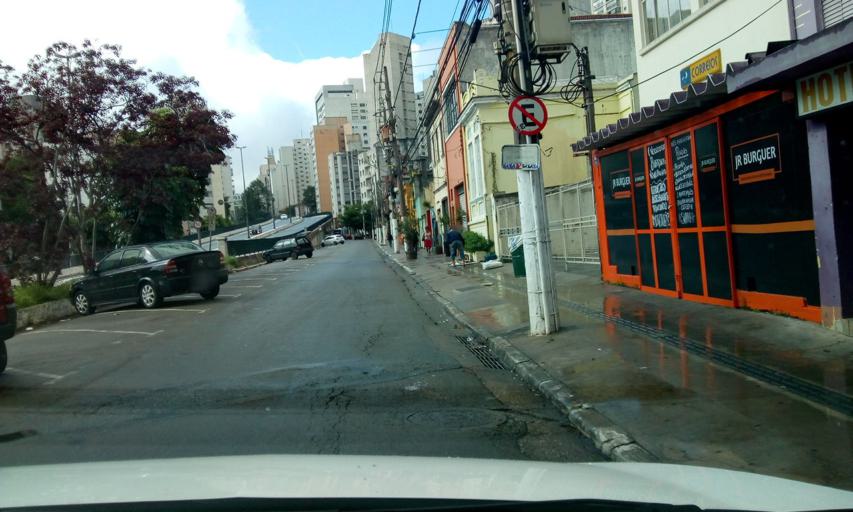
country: BR
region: Sao Paulo
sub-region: Sao Paulo
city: Sao Paulo
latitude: -23.5609
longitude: -46.6462
